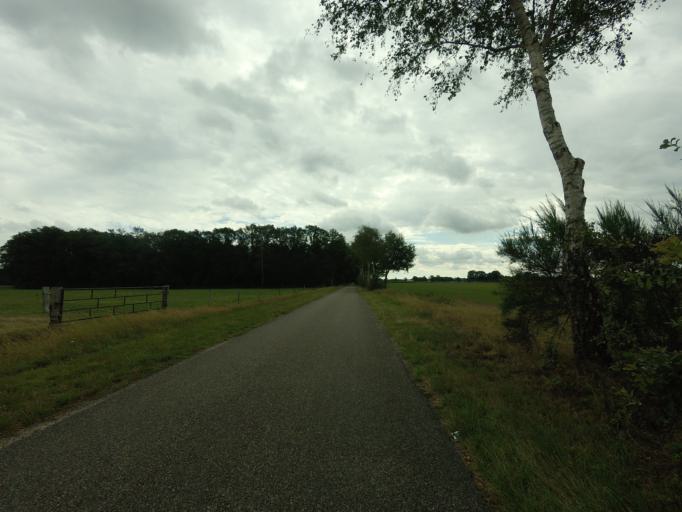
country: NL
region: Gelderland
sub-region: Gemeente Lochem
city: Laren
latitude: 52.3007
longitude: 6.3664
